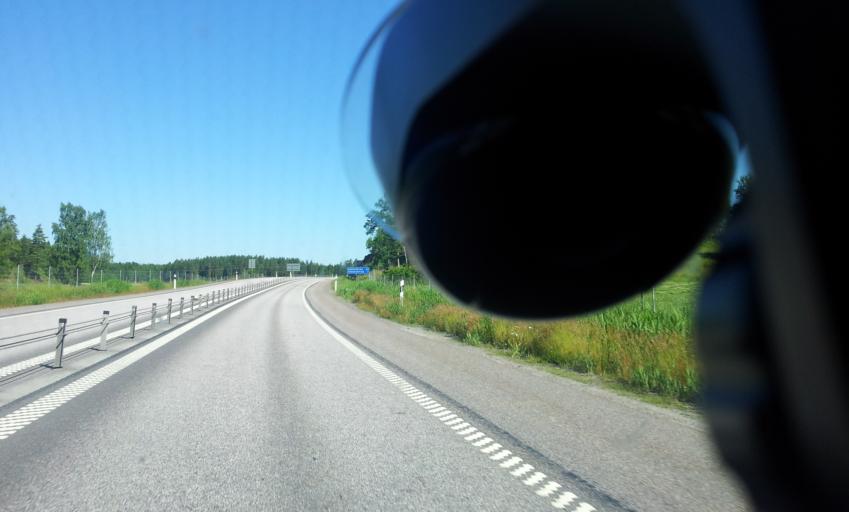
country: SE
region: OEstergoetland
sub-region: Soderkopings Kommun
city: Soederkoeping
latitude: 58.3999
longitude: 16.4052
